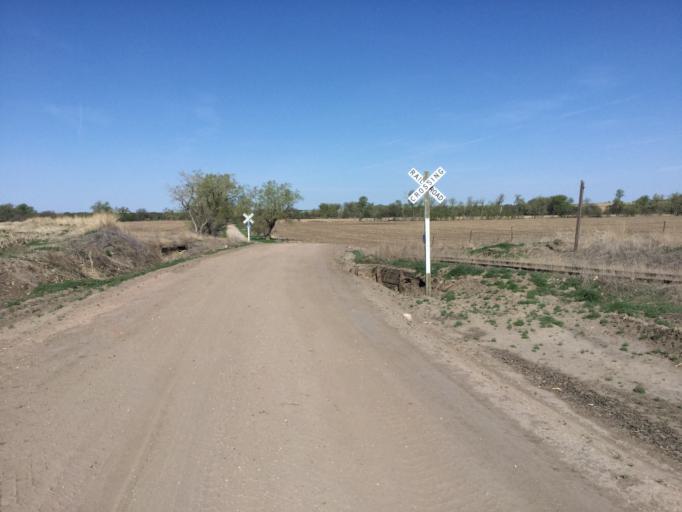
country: US
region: Kansas
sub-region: Decatur County
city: Oberlin
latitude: 40.0019
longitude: -100.5270
